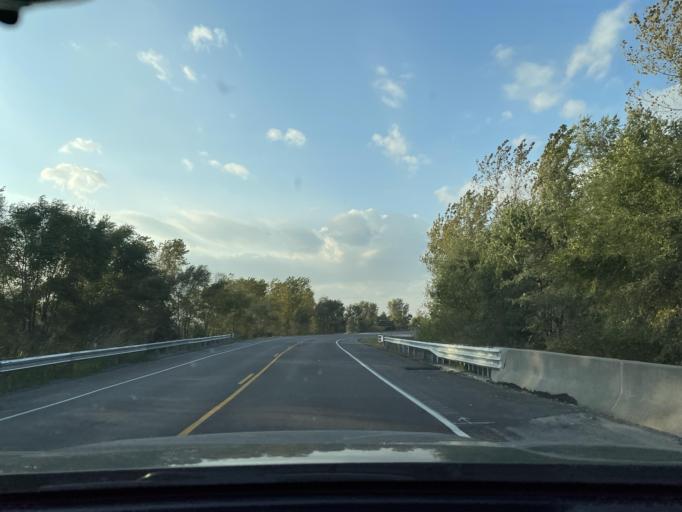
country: US
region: Missouri
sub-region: Andrew County
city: Country Club Village
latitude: 39.8590
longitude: -94.8788
